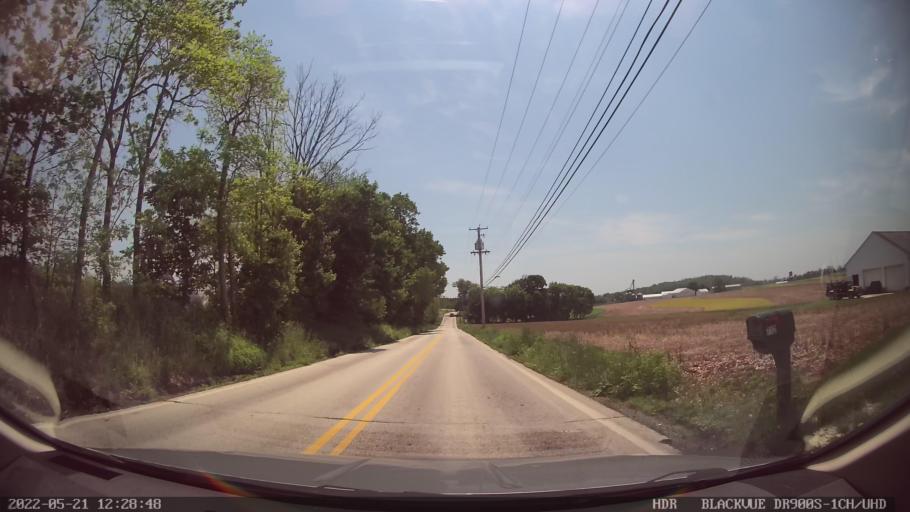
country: US
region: Pennsylvania
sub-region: Berks County
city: Bally
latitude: 40.3669
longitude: -75.5939
